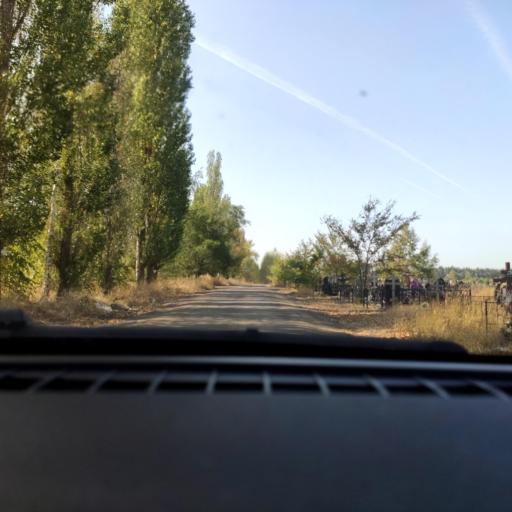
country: RU
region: Voronezj
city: Maslovka
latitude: 51.5131
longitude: 39.1981
